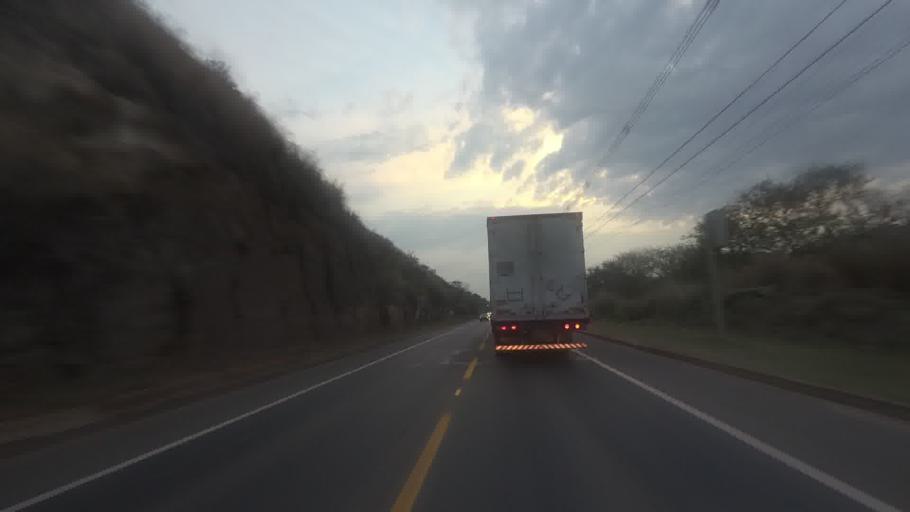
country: BR
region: Minas Gerais
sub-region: Alem Paraiba
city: Alem Paraiba
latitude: -21.8855
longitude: -42.6941
